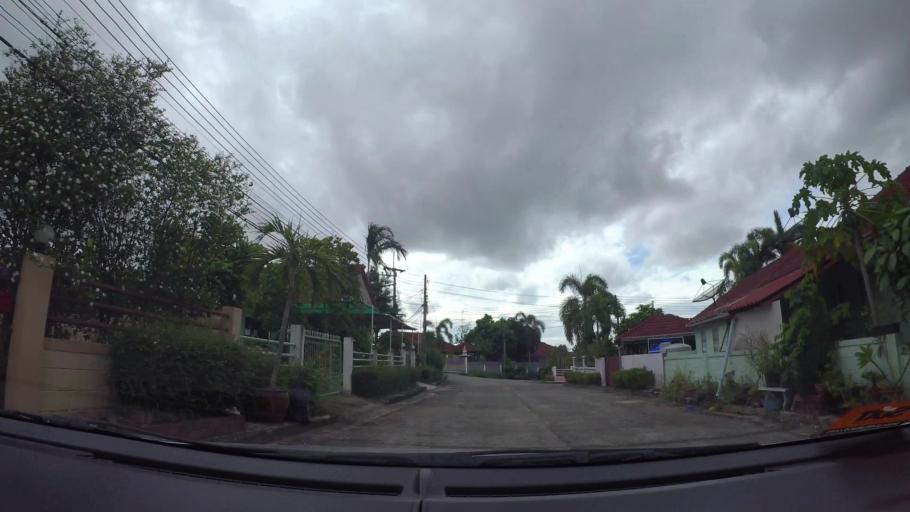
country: TH
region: Chon Buri
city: Sattahip
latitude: 12.7247
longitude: 100.9051
